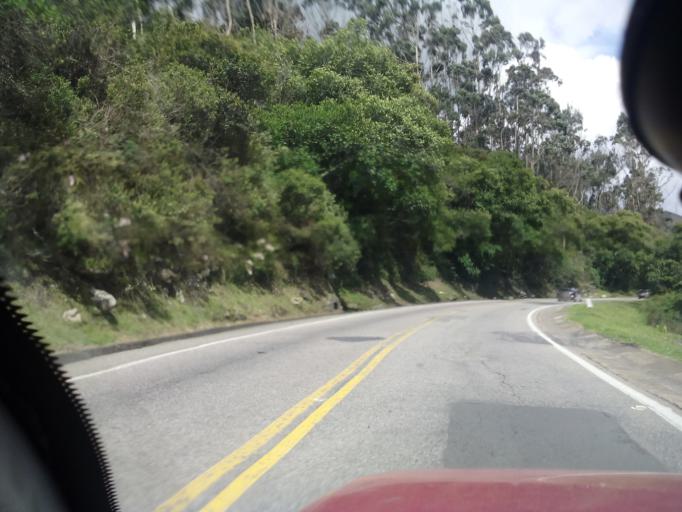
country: CO
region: Boyaca
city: Arcabuco
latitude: 5.7278
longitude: -73.3900
